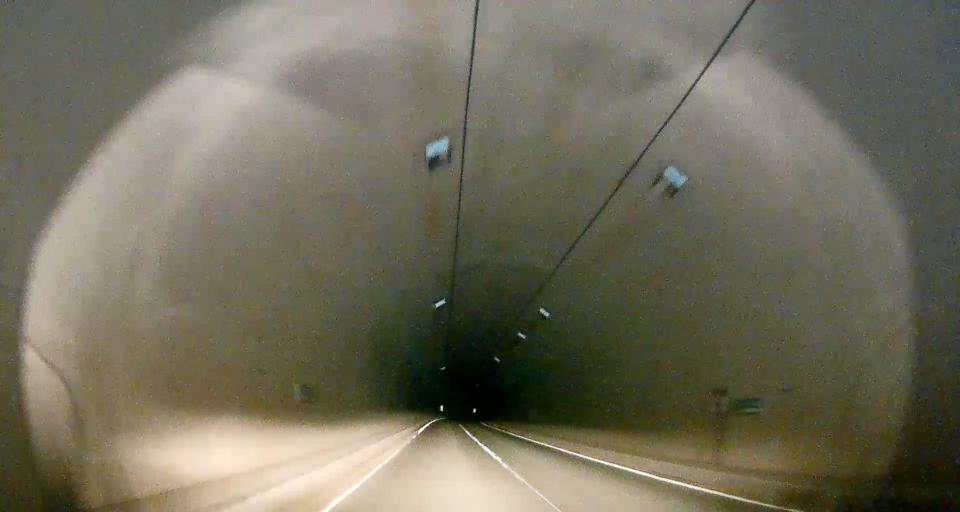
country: JP
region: Hokkaido
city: Chitose
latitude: 42.7882
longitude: 142.0458
